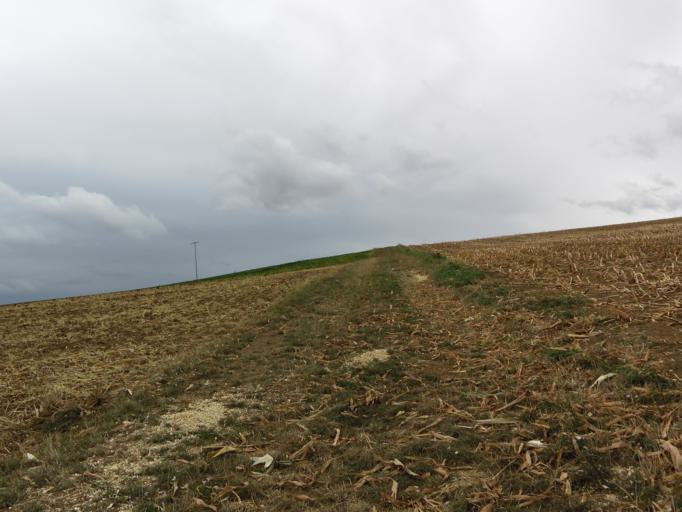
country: DE
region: Bavaria
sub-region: Regierungsbezirk Unterfranken
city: Rimpar
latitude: 49.8564
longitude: 9.9405
